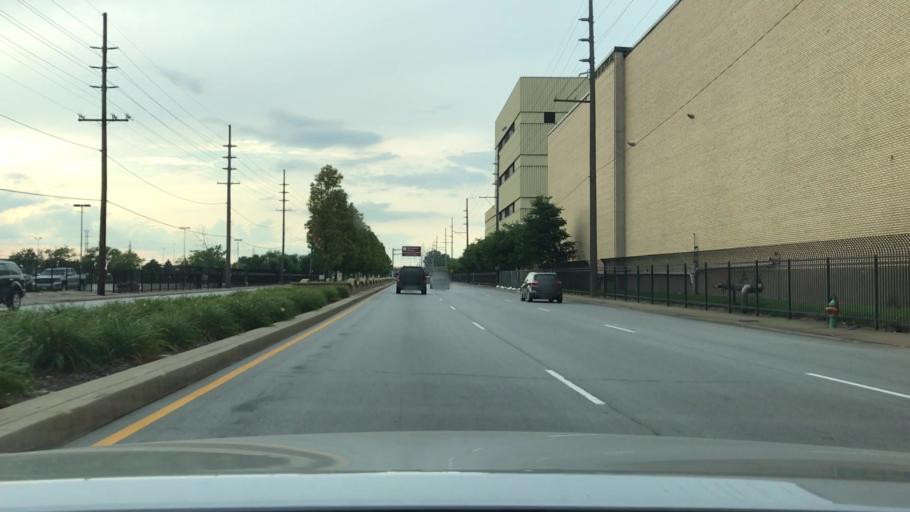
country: US
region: Indiana
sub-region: Lake County
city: Whiting
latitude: 41.6908
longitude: -87.5113
